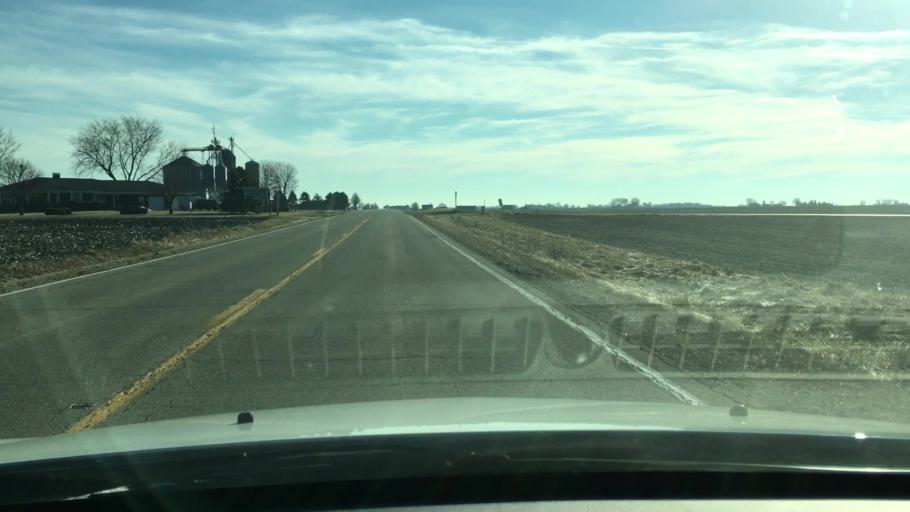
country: US
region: Illinois
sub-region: LaSalle County
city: Mendota
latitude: 41.4992
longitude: -89.1272
